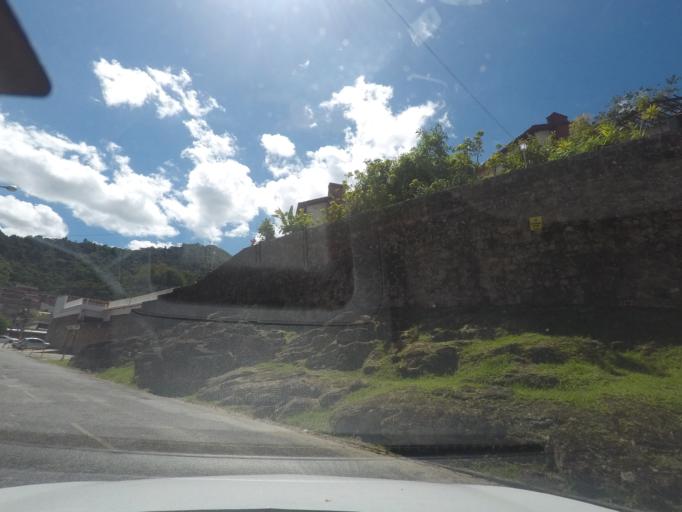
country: BR
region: Rio de Janeiro
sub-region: Teresopolis
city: Teresopolis
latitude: -22.4296
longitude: -42.9786
